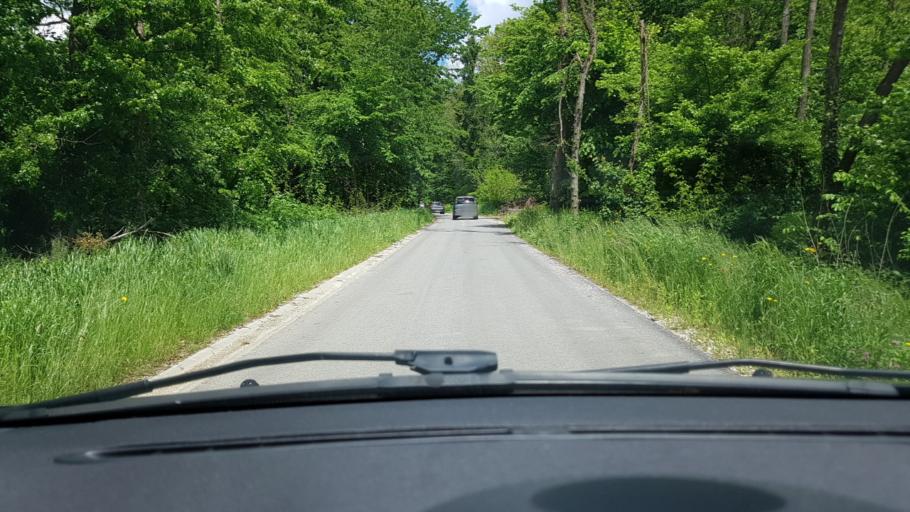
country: HR
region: Krapinsko-Zagorska
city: Pregrada
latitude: 46.1603
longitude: 15.8097
